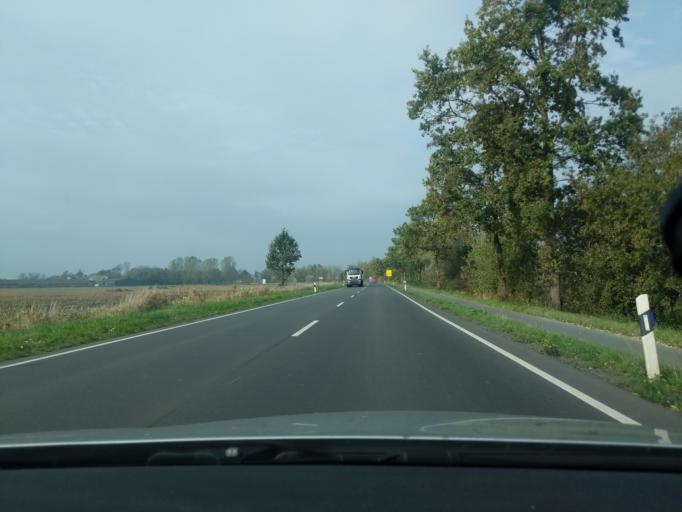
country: DE
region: Lower Saxony
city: Neuhaus an der Oste
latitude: 53.8042
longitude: 9.0217
